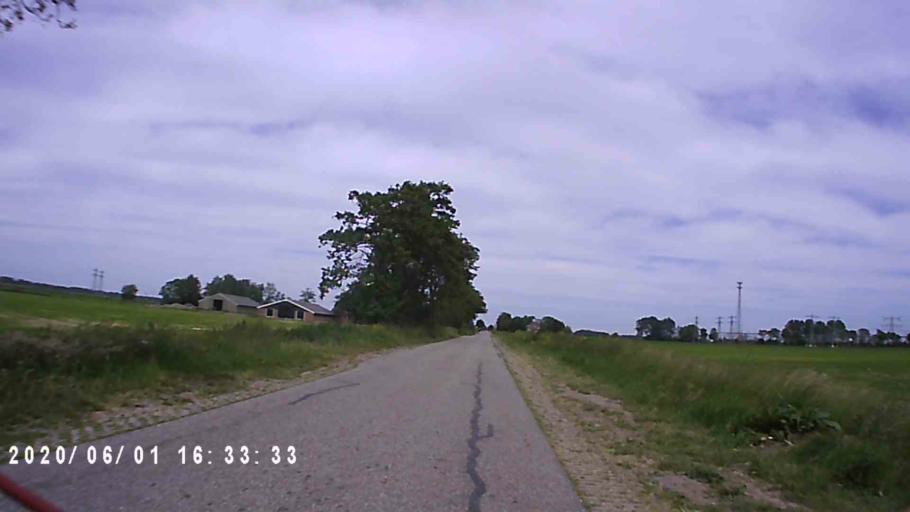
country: NL
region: Friesland
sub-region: Gemeente Leeuwarden
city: Camminghaburen
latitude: 53.1919
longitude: 5.8671
